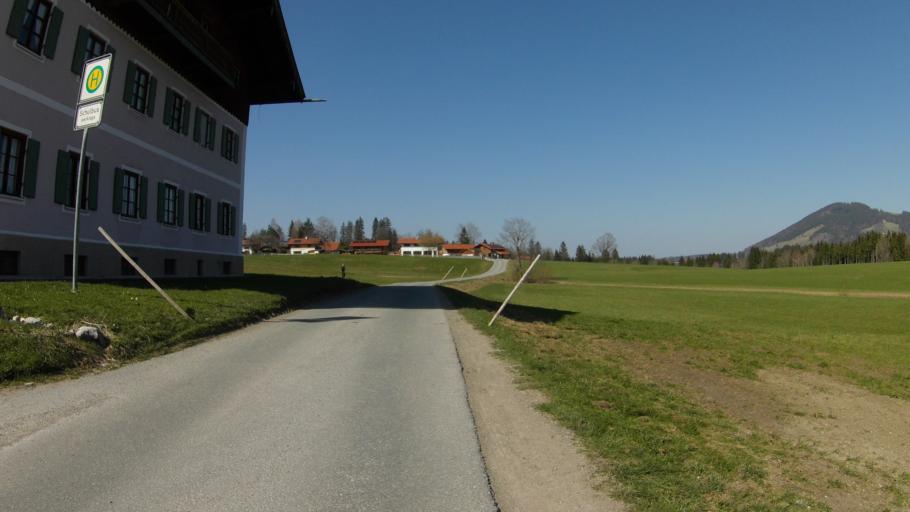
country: DE
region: Bavaria
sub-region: Upper Bavaria
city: Fischbachau
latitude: 47.7230
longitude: 11.9292
